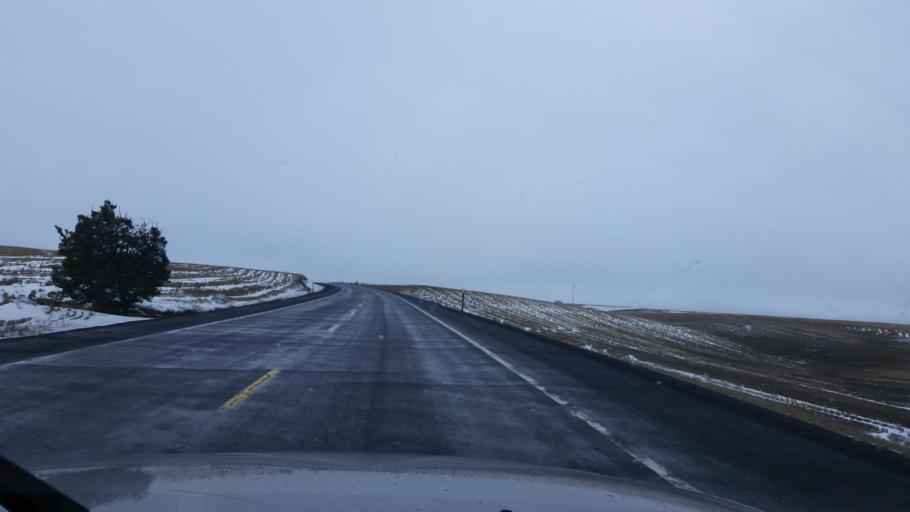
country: US
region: Washington
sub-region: Lincoln County
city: Davenport
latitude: 47.4694
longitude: -118.2937
